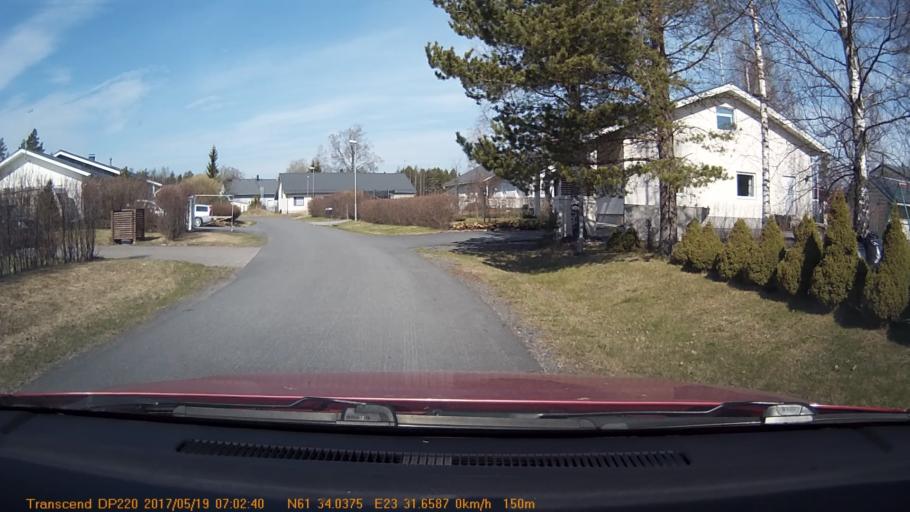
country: FI
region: Pirkanmaa
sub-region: Tampere
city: Yloejaervi
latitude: 61.5673
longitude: 23.5277
